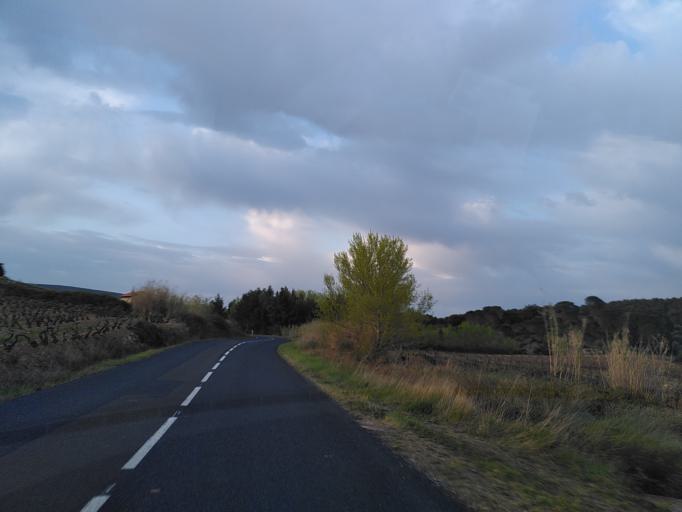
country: FR
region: Languedoc-Roussillon
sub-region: Departement des Pyrenees-Orientales
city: Estagel
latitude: 42.8039
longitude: 2.6986
